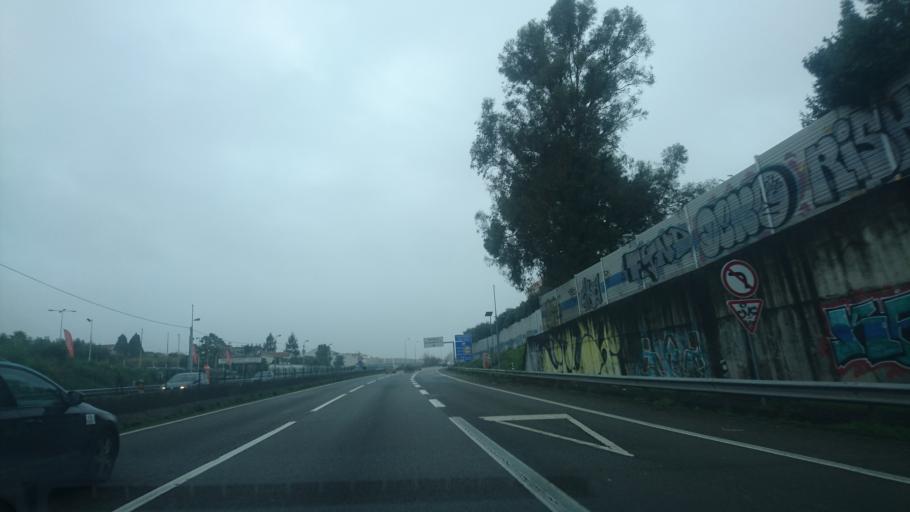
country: PT
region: Porto
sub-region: Vila Nova de Gaia
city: Vilar do Paraiso
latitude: 41.1022
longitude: -8.6265
